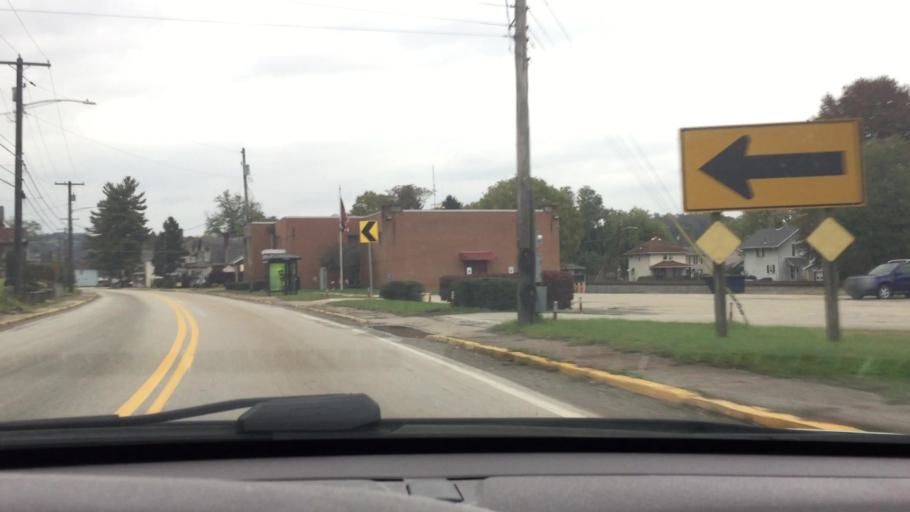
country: US
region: Pennsylvania
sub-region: Fayette County
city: Fairhope
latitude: 40.0960
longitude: -79.8443
